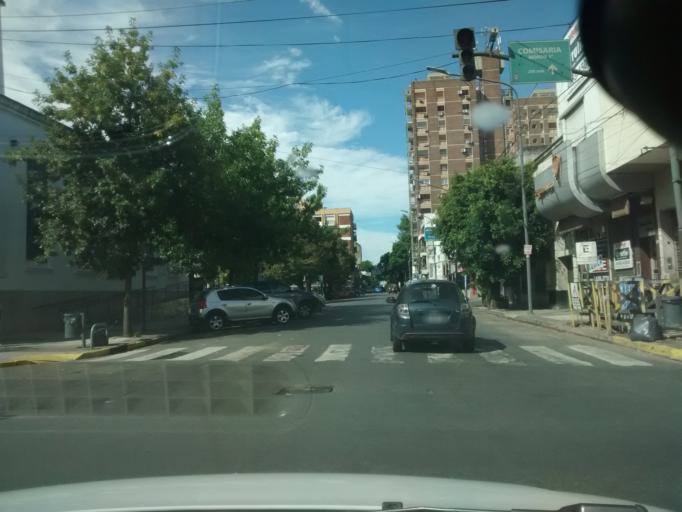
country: AR
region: Buenos Aires
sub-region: Partido de Moron
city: Moron
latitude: -34.6502
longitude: -58.6229
